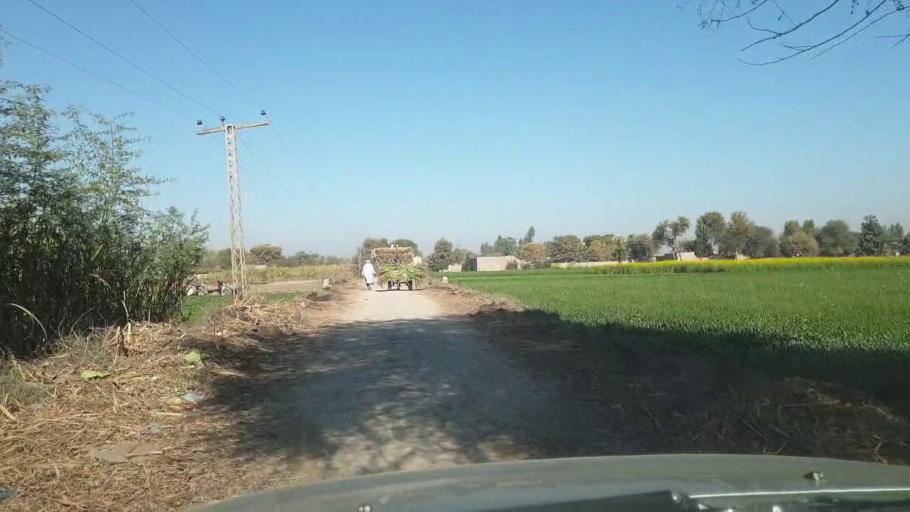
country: PK
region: Sindh
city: Ghotki
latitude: 28.0945
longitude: 69.3429
